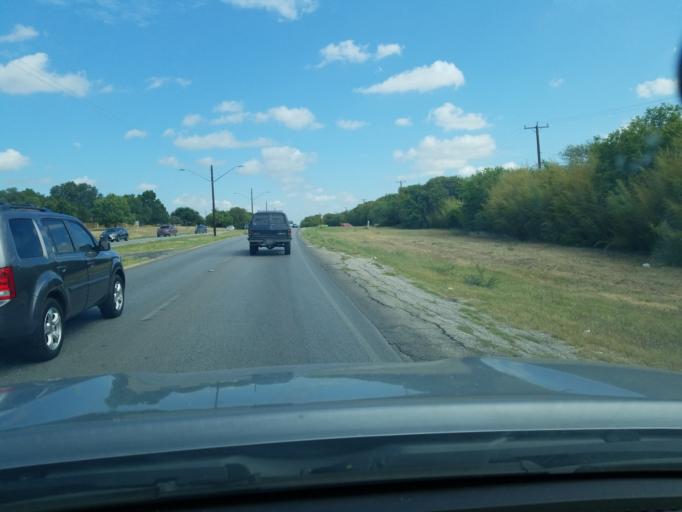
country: US
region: Texas
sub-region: Bexar County
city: Terrell Hills
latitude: 29.4967
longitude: -98.4345
